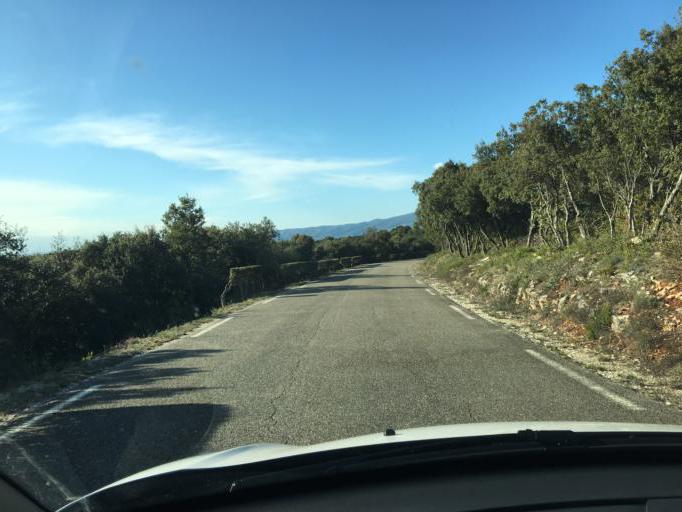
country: FR
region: Provence-Alpes-Cote d'Azur
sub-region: Departement du Vaucluse
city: Villes-sur-Auzon
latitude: 44.0392
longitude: 5.2559
